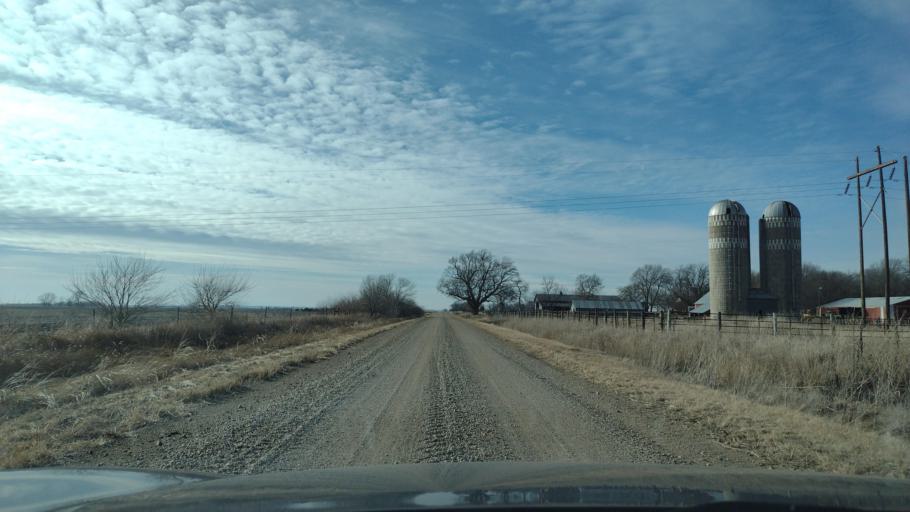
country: US
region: South Dakota
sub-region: Union County
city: Beresford
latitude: 42.9390
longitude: -96.8117
